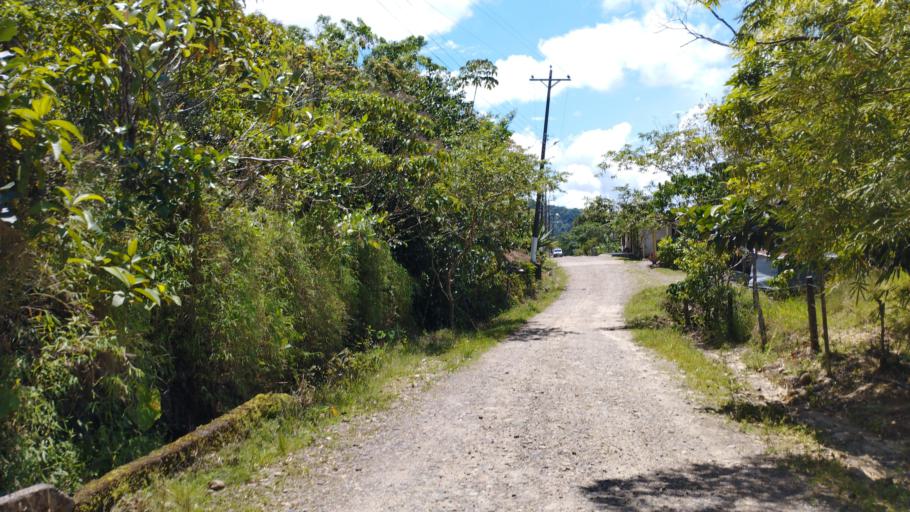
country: CO
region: Boyaca
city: San Luis de Gaceno
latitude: 4.7489
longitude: -73.1462
